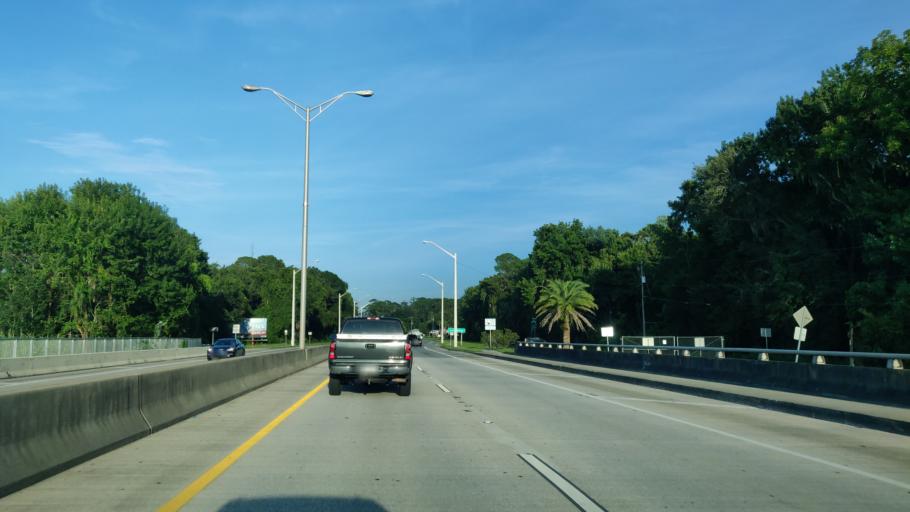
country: US
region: Florida
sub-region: Putnam County
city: Palatka
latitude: 29.6441
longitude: -81.6160
